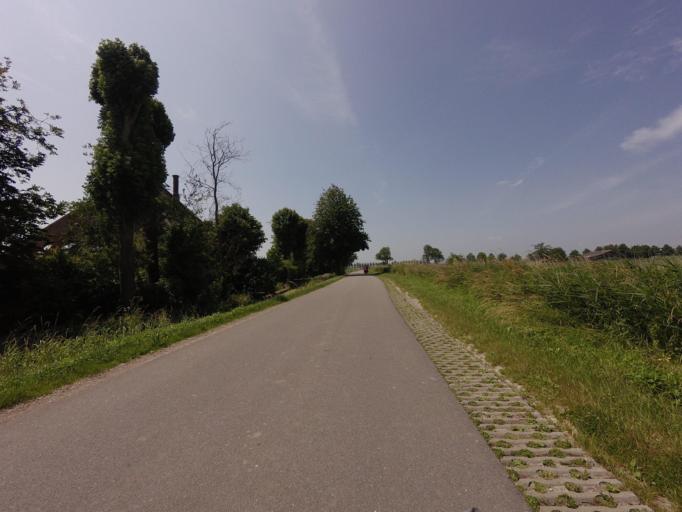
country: NL
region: North Holland
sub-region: Gemeente Heerhugowaard
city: Heerhugowaard
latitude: 52.6448
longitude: 4.8932
